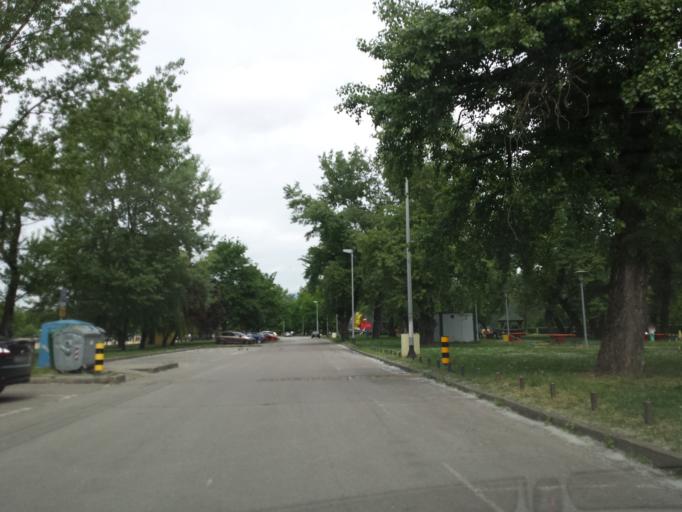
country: HR
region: Grad Zagreb
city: Jankomir
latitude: 45.7784
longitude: 15.9377
